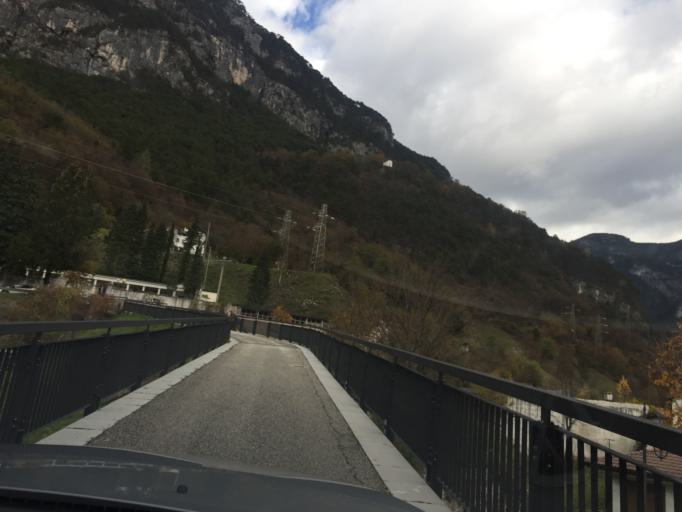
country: IT
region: Friuli Venezia Giulia
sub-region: Provincia di Udine
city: Chiusaforte
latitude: 46.4083
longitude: 13.3087
